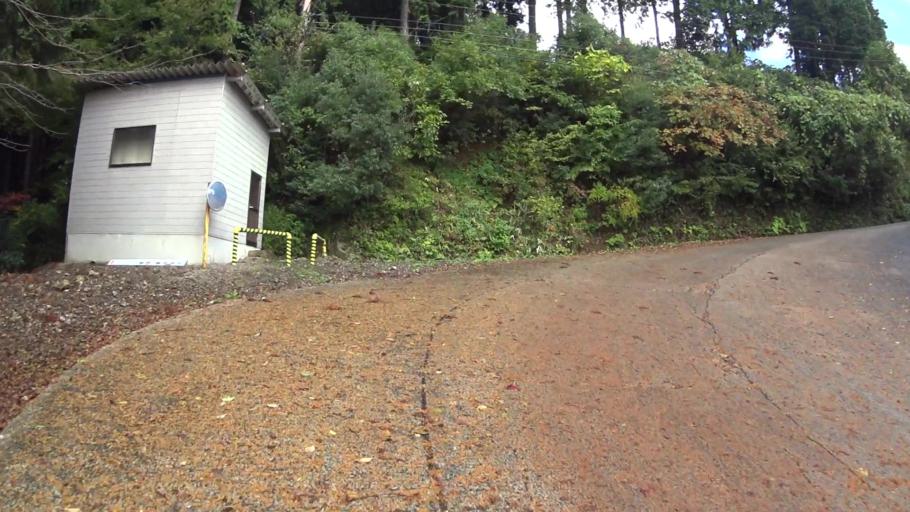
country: JP
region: Kyoto
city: Miyazu
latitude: 35.5955
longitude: 135.1857
